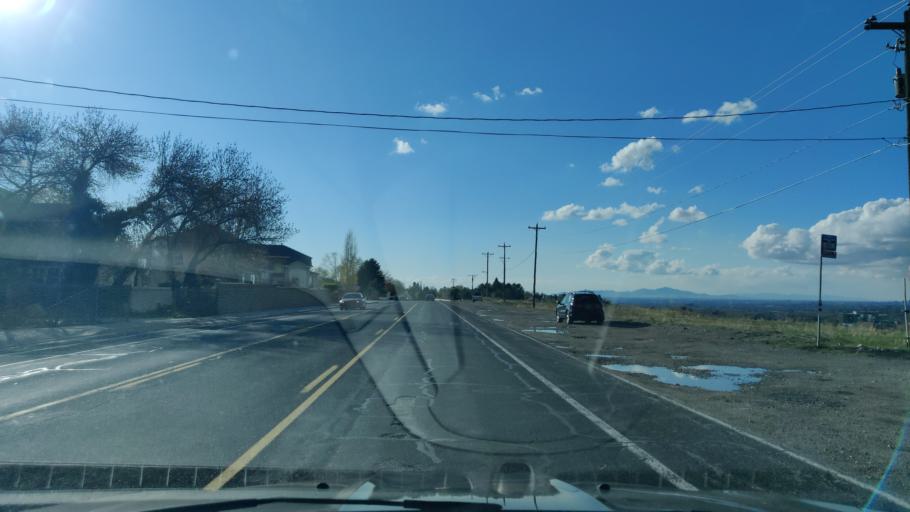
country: US
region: Utah
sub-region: Salt Lake County
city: Cottonwood Heights
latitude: 40.6216
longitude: -111.7978
